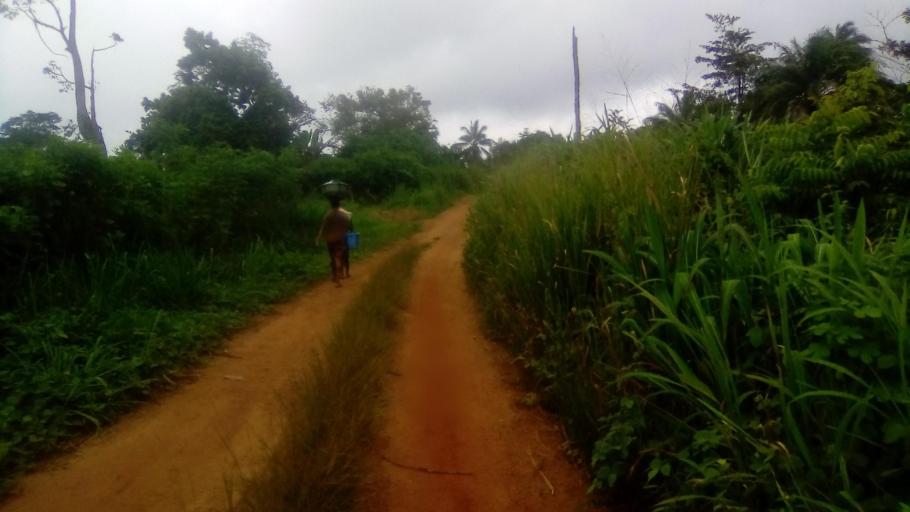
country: SL
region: Eastern Province
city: Kailahun
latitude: 8.3055
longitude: -10.5599
